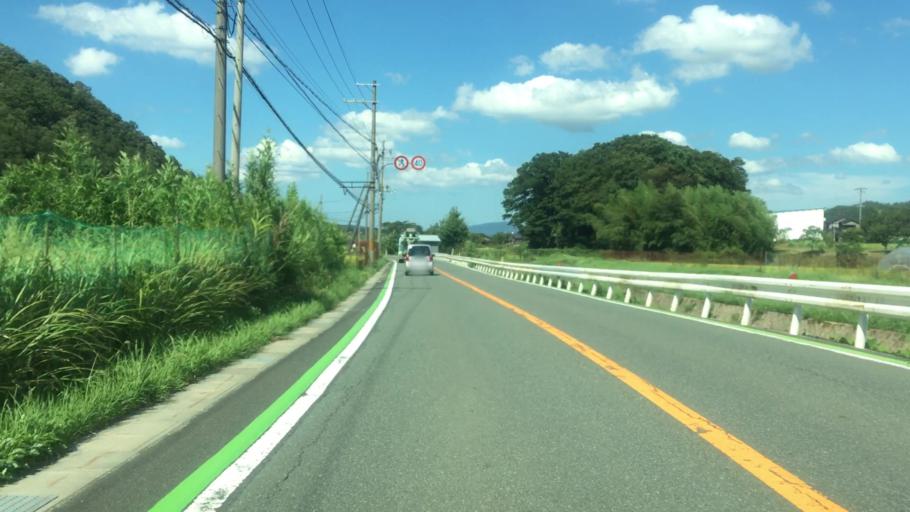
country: JP
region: Kyoto
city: Miyazu
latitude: 35.5825
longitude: 135.0350
